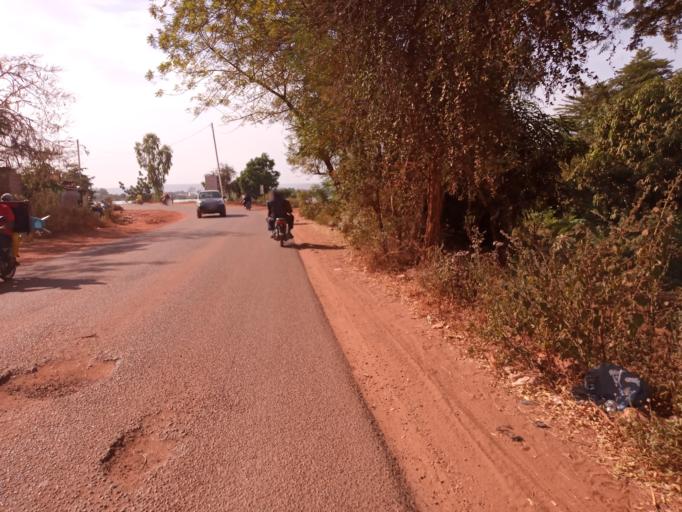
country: ML
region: Bamako
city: Bamako
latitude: 12.6297
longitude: -7.9514
